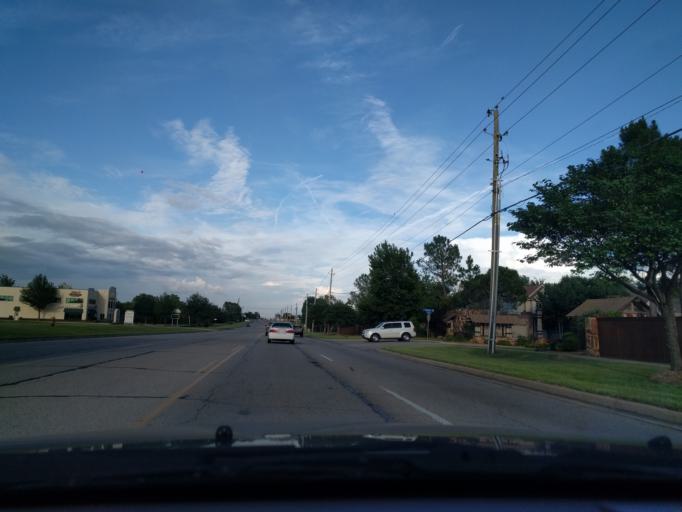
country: US
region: Oklahoma
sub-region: Tulsa County
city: Broken Arrow
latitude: 36.0609
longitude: -95.8256
